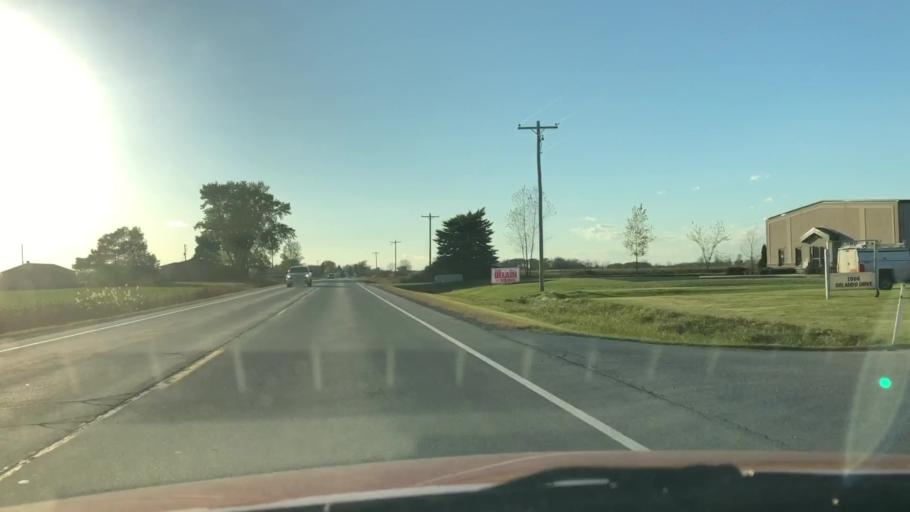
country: US
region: Wisconsin
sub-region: Brown County
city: Oneida
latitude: 44.4446
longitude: -88.1439
